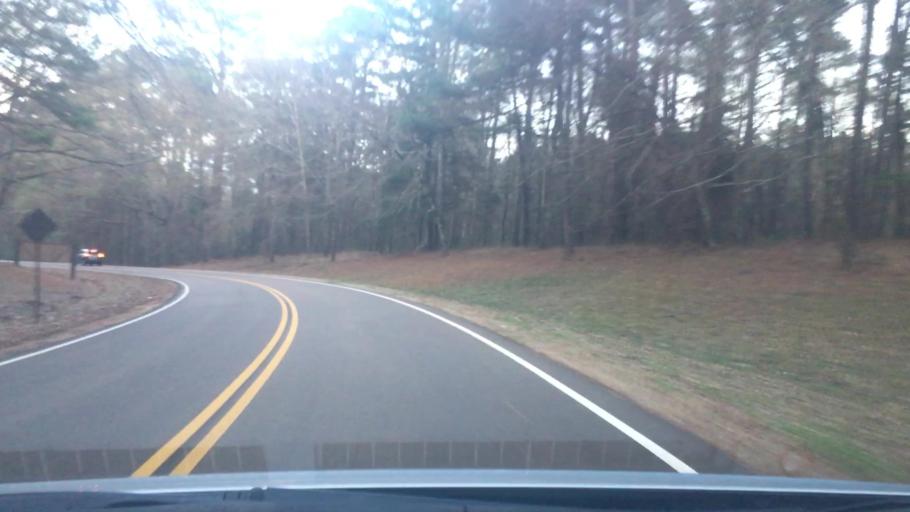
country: US
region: Mississippi
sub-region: Madison County
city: Canton
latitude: 32.5227
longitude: -89.9750
